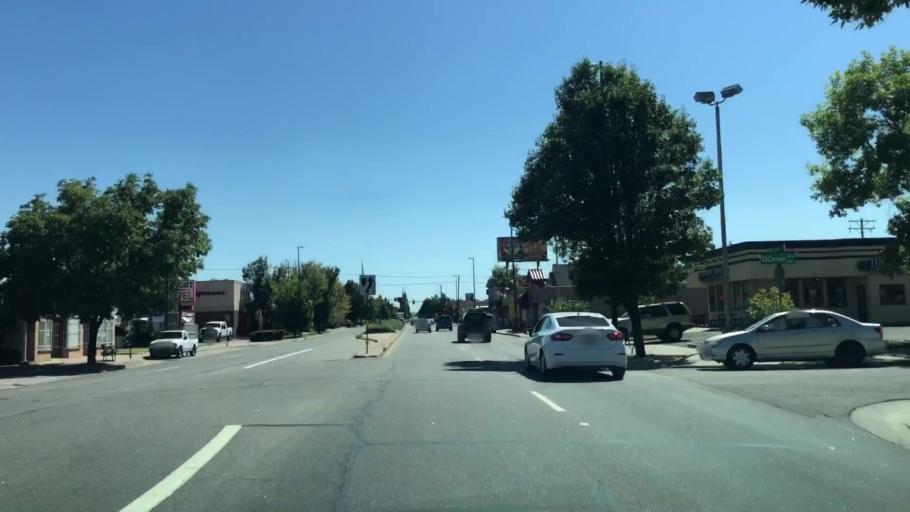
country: US
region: Colorado
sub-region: Arapahoe County
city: Englewood
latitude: 39.6624
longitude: -104.9877
